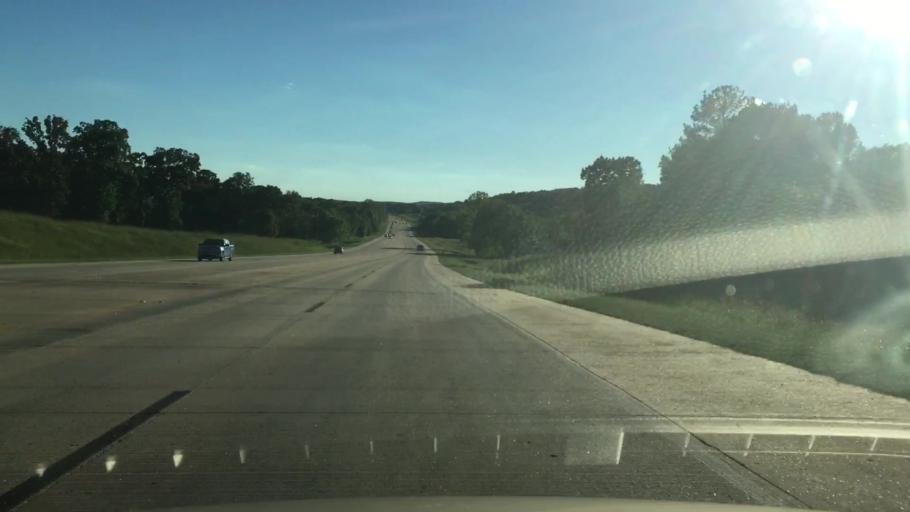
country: US
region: Oklahoma
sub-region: Cherokee County
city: Park Hill
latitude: 35.8440
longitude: -95.0301
